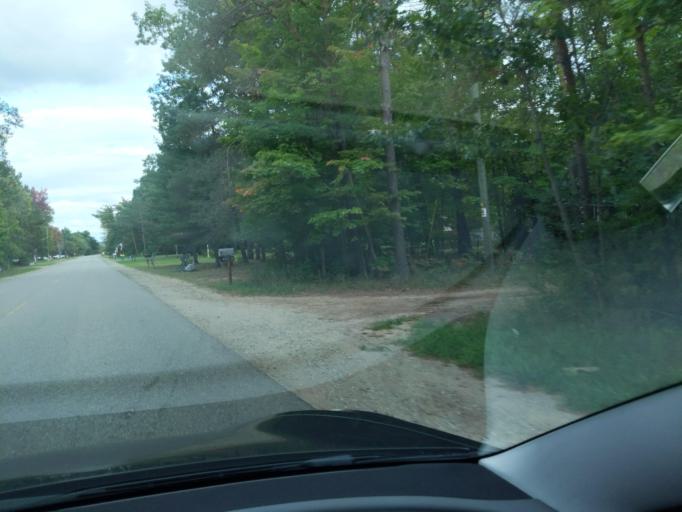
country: US
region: Michigan
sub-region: Kalkaska County
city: Rapid City
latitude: 44.8400
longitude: -85.2977
